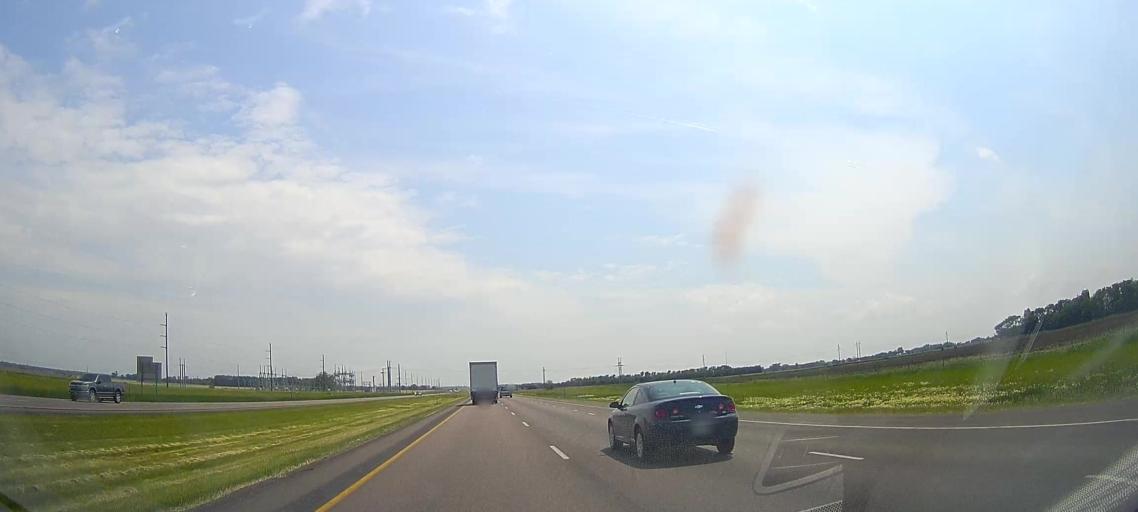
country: US
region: South Dakota
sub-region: Union County
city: Beresford
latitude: 43.1233
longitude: -96.7969
